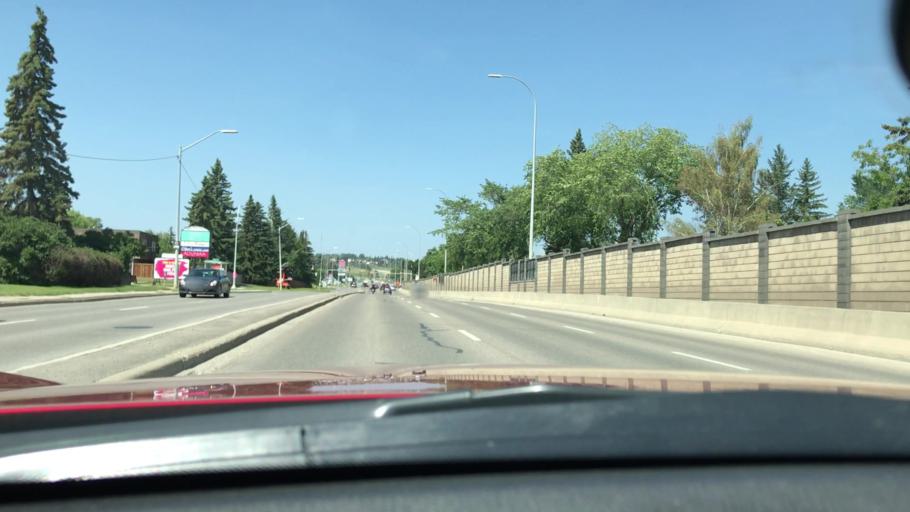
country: CA
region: Alberta
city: Calgary
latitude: 51.0473
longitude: -114.1480
